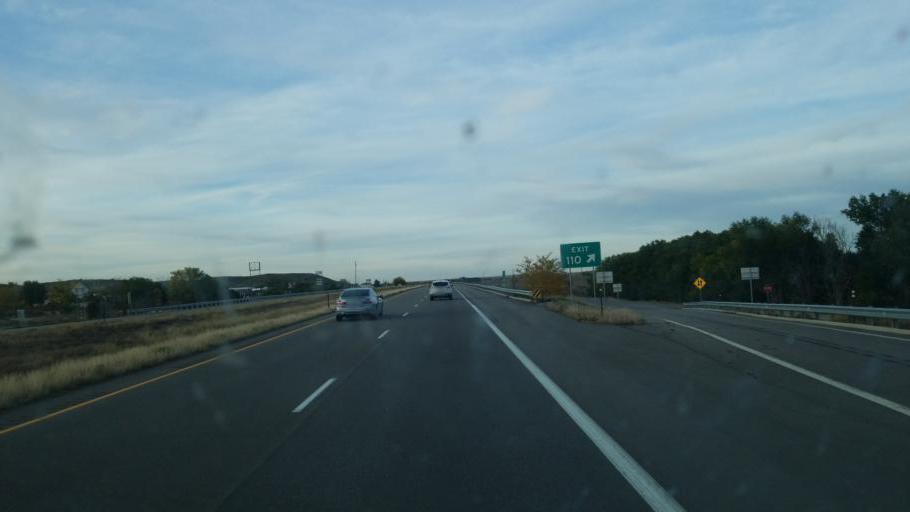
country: US
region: Colorado
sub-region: Pueblo County
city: Pueblo West
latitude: 38.4290
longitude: -104.6074
